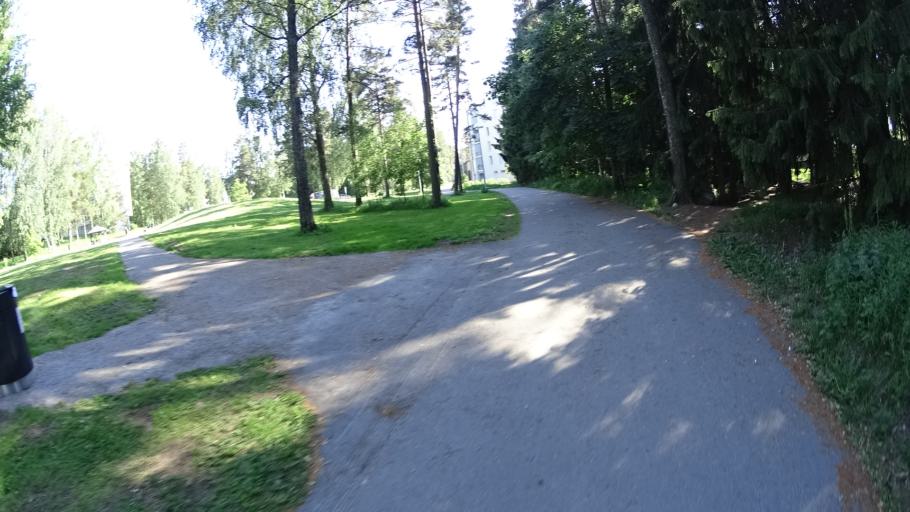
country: FI
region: Uusimaa
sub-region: Helsinki
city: Vantaa
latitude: 60.2225
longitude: 25.1423
